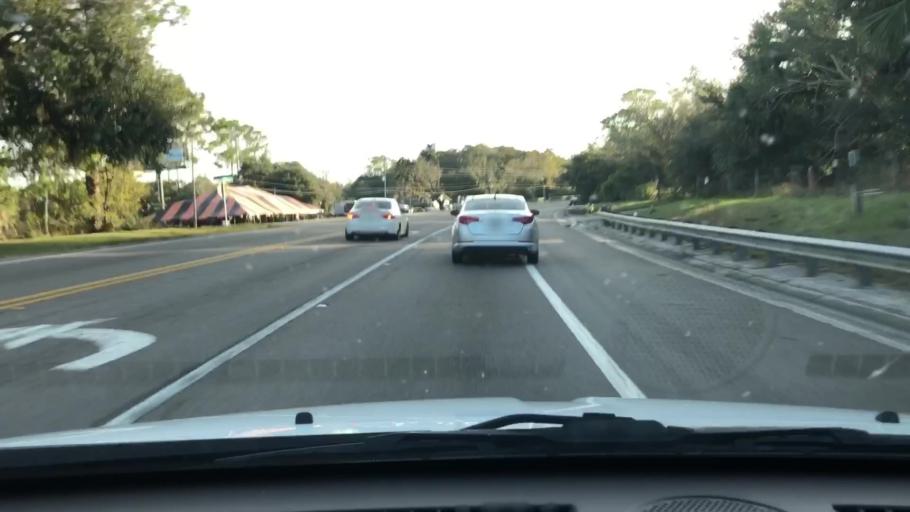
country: US
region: Florida
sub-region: Polk County
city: Loughman
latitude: 28.2646
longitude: -81.5335
